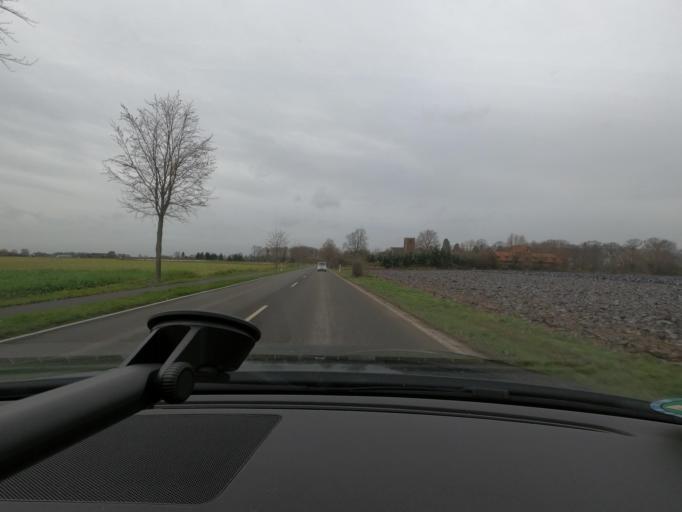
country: DE
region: North Rhine-Westphalia
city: Kempen
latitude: 51.3526
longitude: 6.4576
